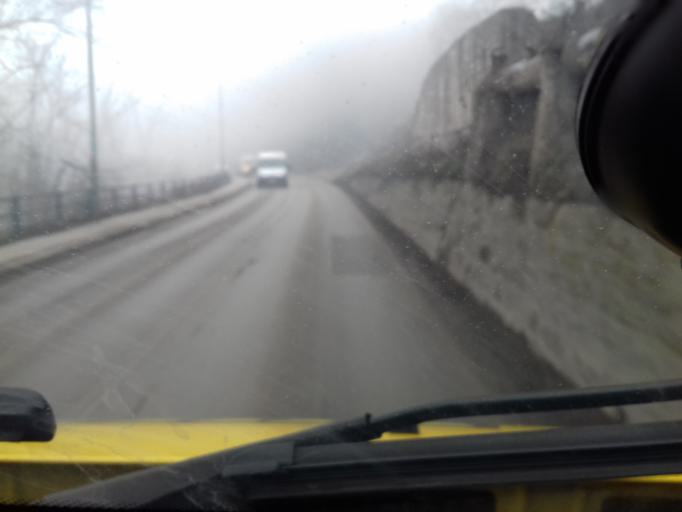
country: BA
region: Federation of Bosnia and Herzegovina
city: Visoko
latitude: 43.9977
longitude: 18.1654
